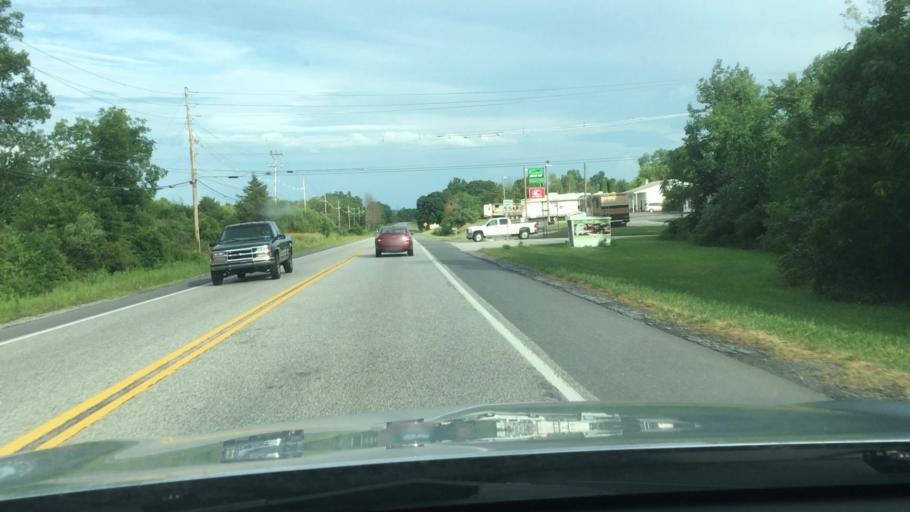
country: US
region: Pennsylvania
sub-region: York County
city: Dillsburg
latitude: 40.0906
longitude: -76.9515
